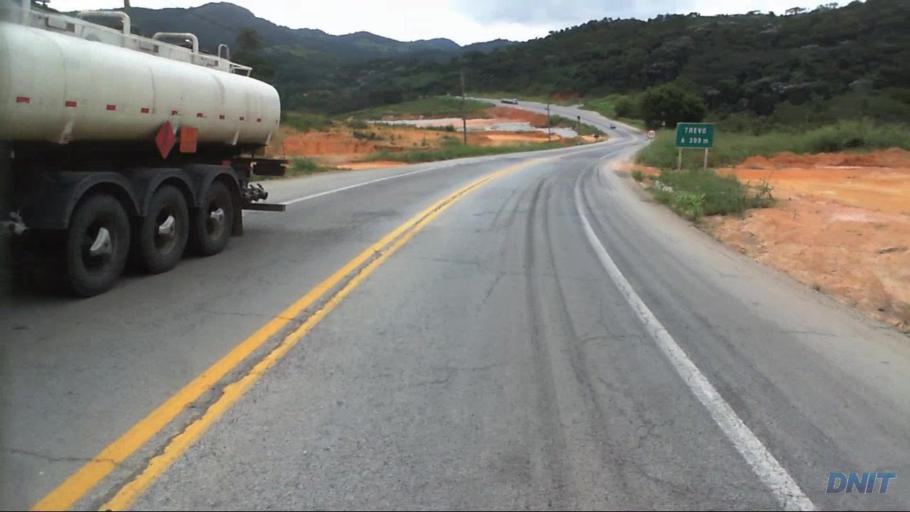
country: BR
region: Minas Gerais
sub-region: Barao De Cocais
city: Barao de Cocais
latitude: -19.7428
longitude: -43.5047
